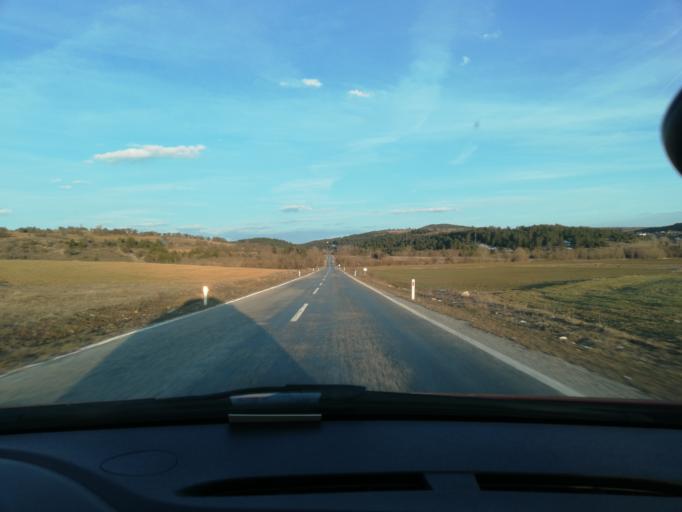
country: TR
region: Kastamonu
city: Agli
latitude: 41.6953
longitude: 33.6130
